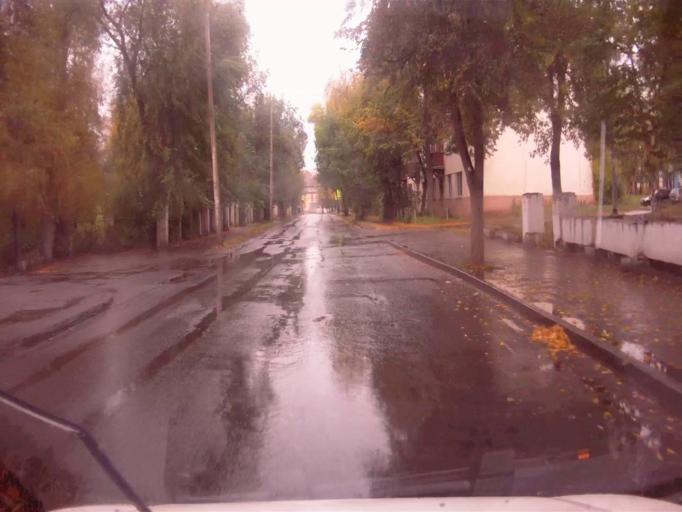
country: RU
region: Chelyabinsk
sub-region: Gorod Chelyabinsk
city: Chelyabinsk
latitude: 55.1923
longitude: 61.4119
